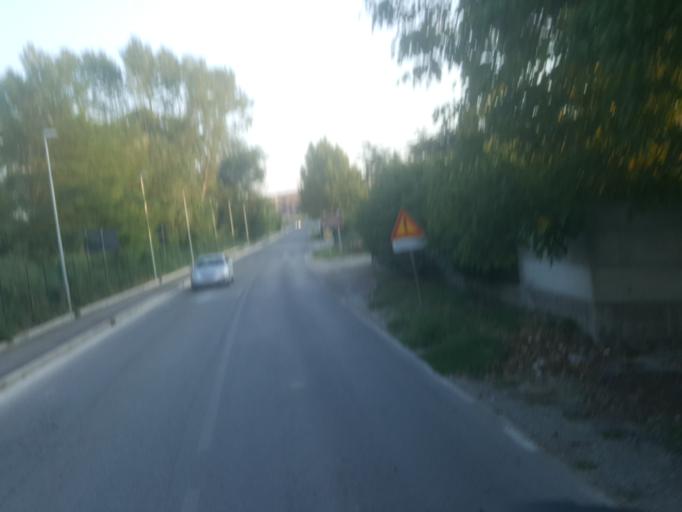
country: IT
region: Tuscany
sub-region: Province of Florence
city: Certaldo
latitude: 43.5436
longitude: 11.0337
